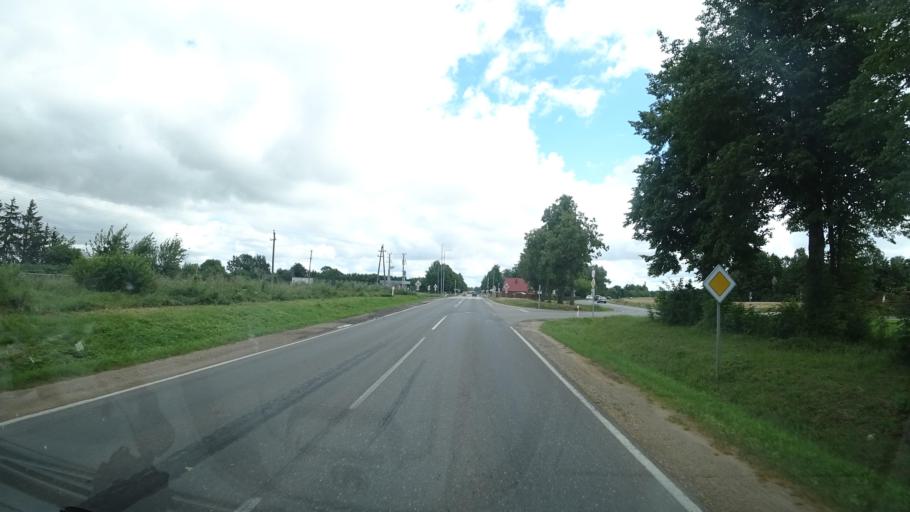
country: LT
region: Marijampoles apskritis
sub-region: Marijampole Municipality
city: Marijampole
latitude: 54.5261
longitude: 23.3254
